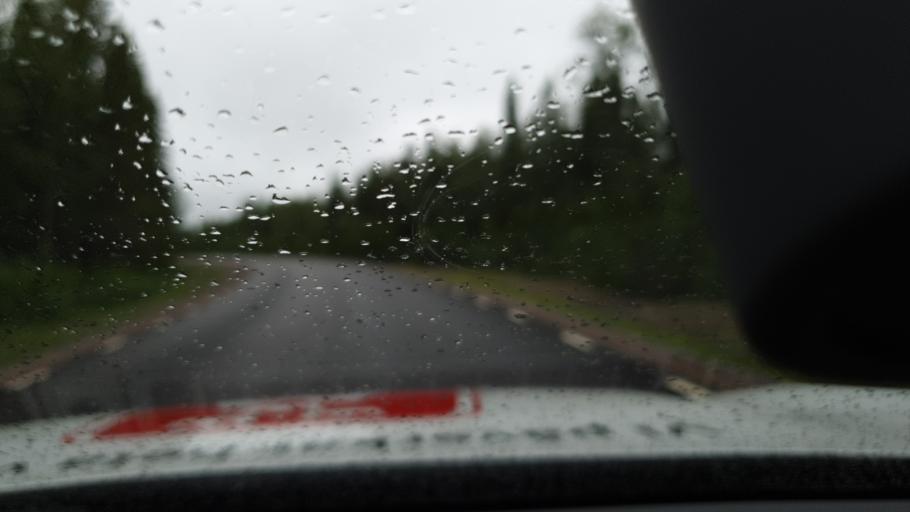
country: SE
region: Norrbotten
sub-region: Overtornea Kommun
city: OEvertornea
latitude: 66.4947
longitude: 23.4388
